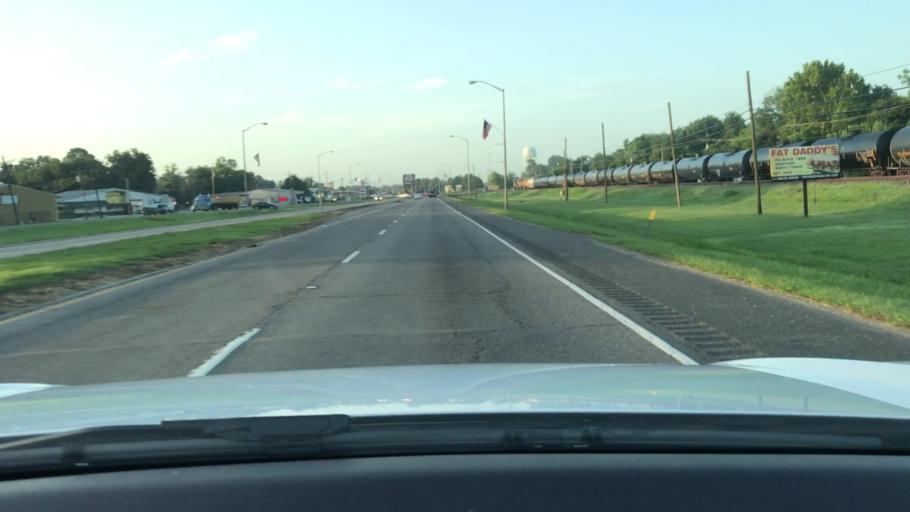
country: US
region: Louisiana
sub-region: Iberville Parish
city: Plaquemine
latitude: 30.3012
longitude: -91.2431
